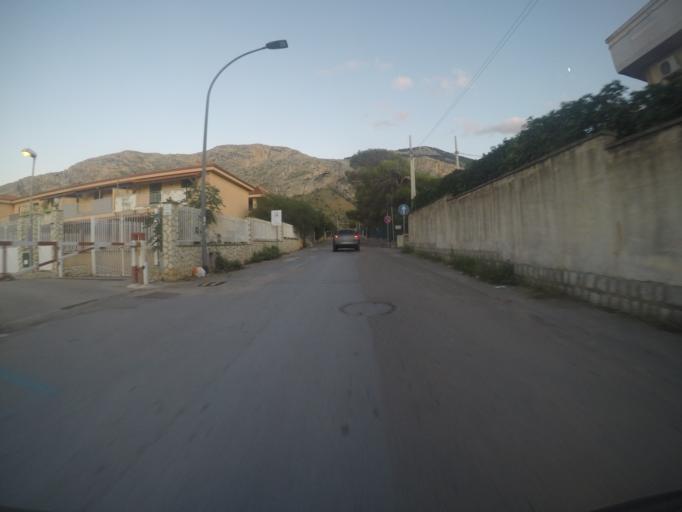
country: IT
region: Sicily
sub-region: Palermo
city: Isola delle Femmine
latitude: 38.1859
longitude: 13.2396
